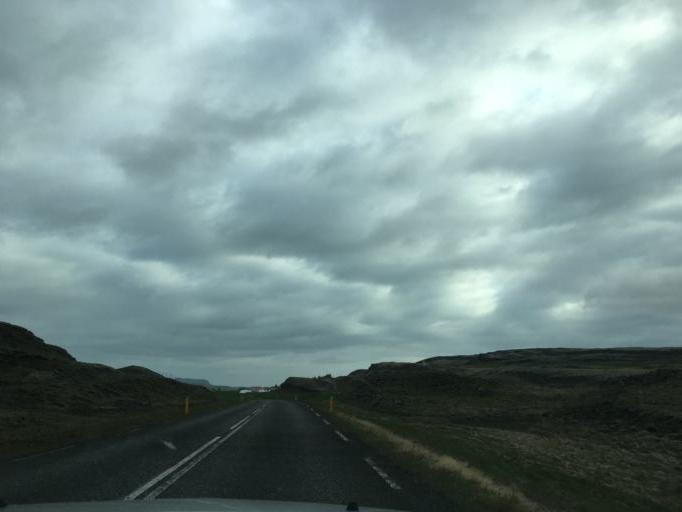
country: IS
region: South
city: Vestmannaeyjar
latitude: 64.2051
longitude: -20.2733
